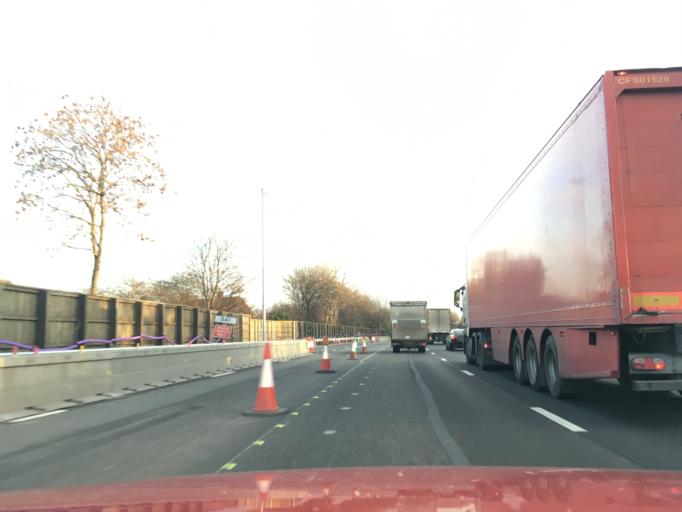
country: GB
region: England
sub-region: Staffordshire
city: Stafford
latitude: 52.7832
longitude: -2.1251
